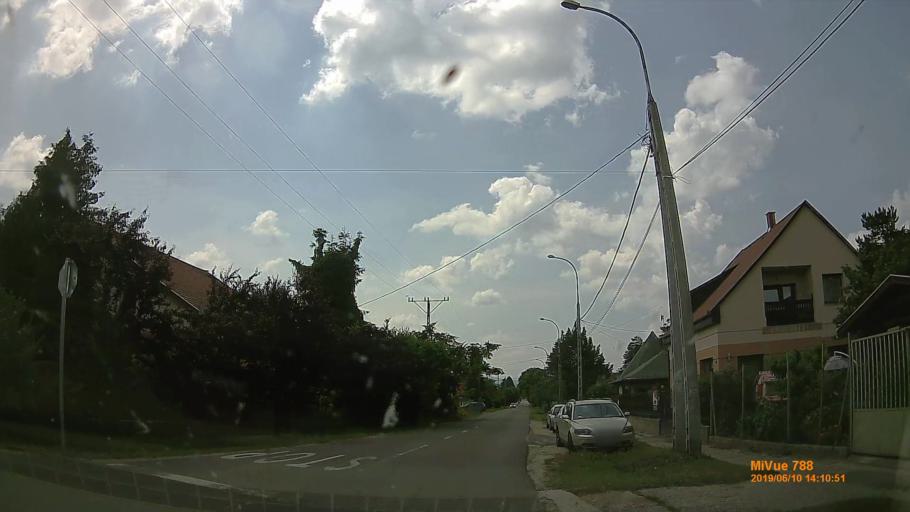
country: HU
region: Pest
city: God
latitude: 47.6771
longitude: 19.1423
